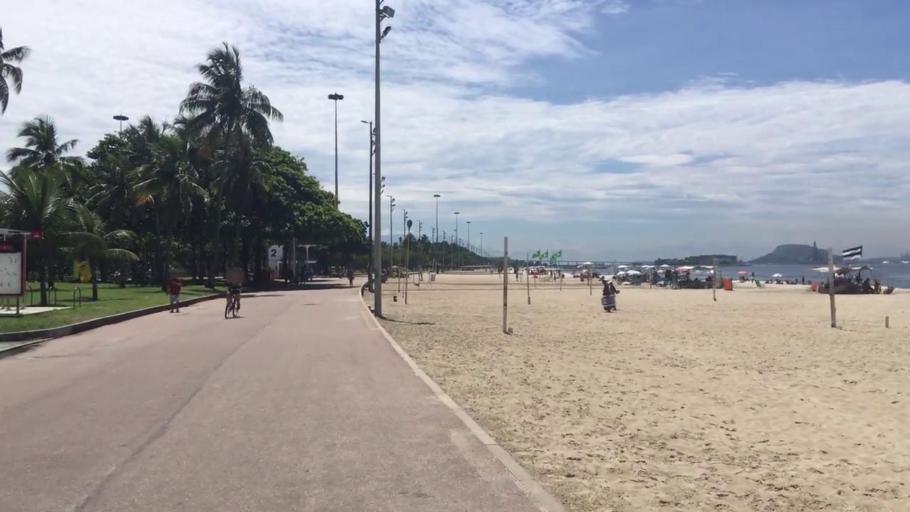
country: BR
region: Rio de Janeiro
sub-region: Rio De Janeiro
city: Rio de Janeiro
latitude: -22.9307
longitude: -43.1719
